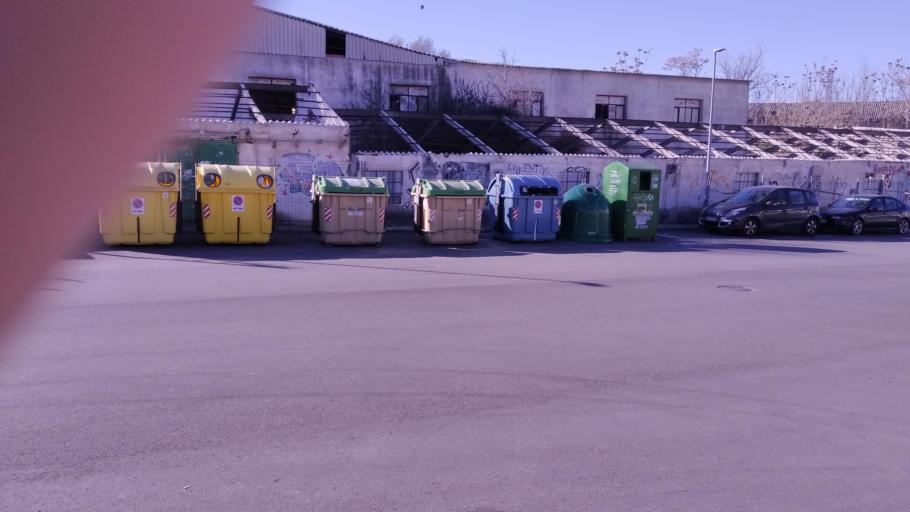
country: ES
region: Castille-La Mancha
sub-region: Province of Toledo
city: Esquivias
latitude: 40.1018
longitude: -3.7657
